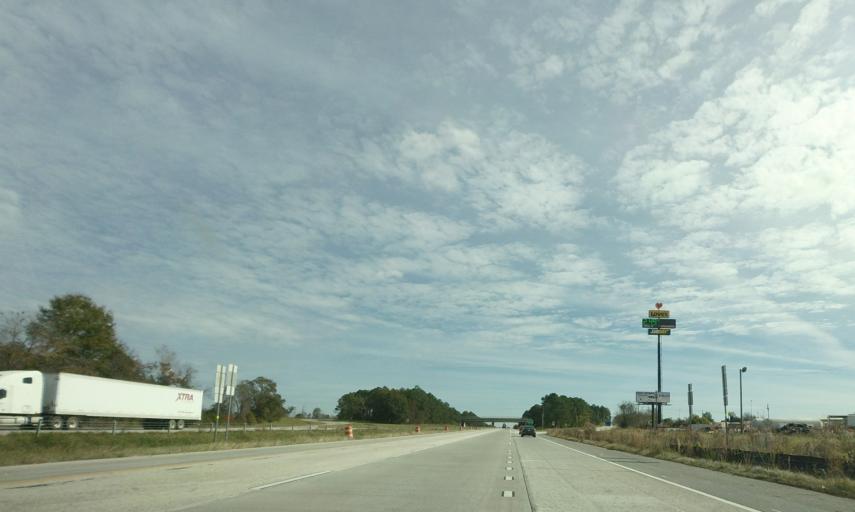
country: US
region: Georgia
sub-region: Laurens County
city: Dublin
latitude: 32.4981
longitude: -82.9835
